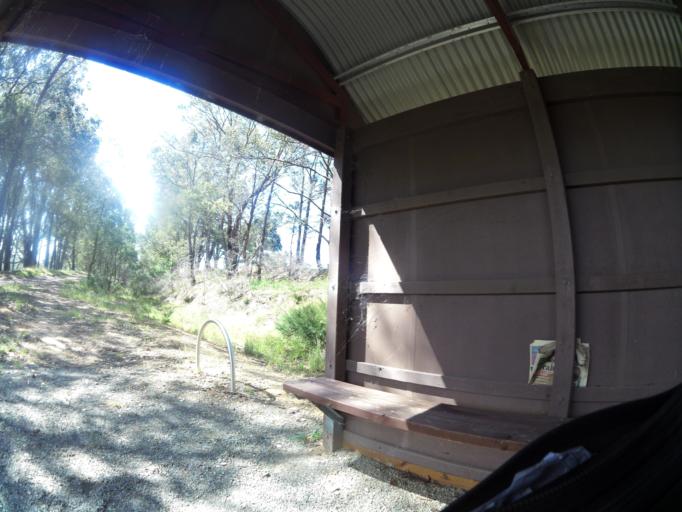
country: AU
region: Victoria
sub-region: East Gippsland
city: Lakes Entrance
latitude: -37.7337
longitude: 148.1626
